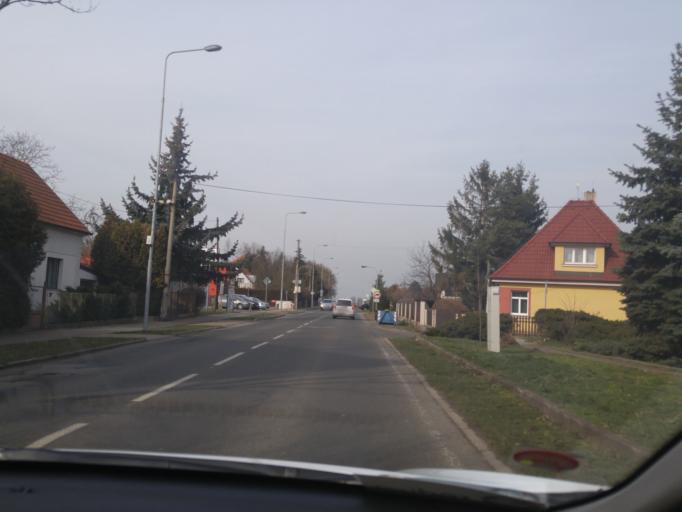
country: CZ
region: Central Bohemia
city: Brandys nad Labem-Stara Boleslav
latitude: 50.1896
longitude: 14.6508
